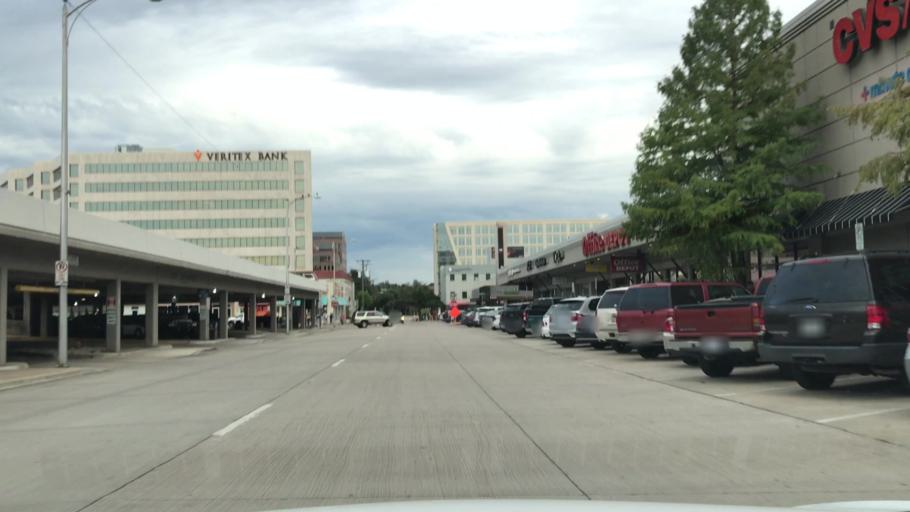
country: US
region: Texas
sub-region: Dallas County
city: University Park
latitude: 32.8646
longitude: -96.8065
